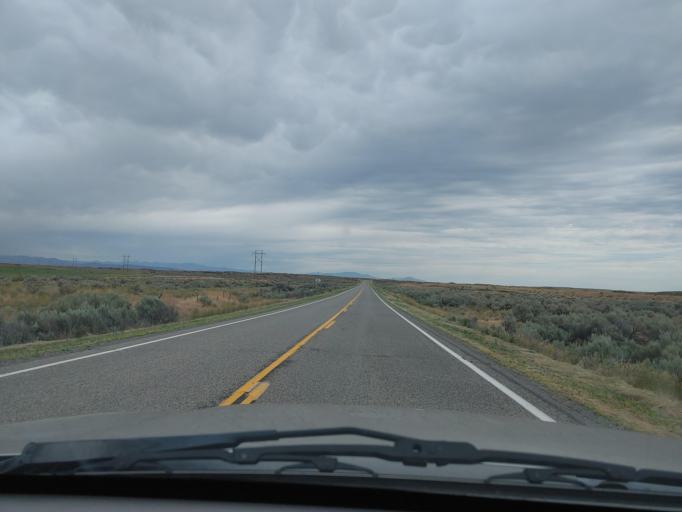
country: US
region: Idaho
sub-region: Lincoln County
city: Shoshone
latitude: 43.0859
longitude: -114.0965
